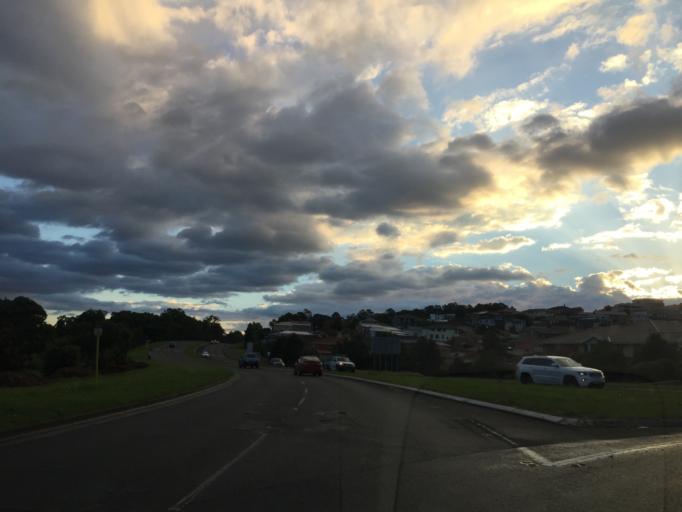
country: AU
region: New South Wales
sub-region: Shellharbour
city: Albion Park Rail
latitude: -34.5707
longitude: 150.8233
